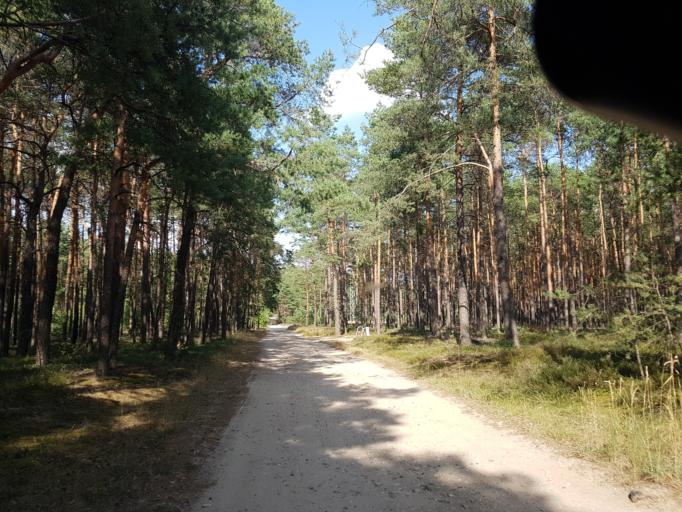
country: DE
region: Brandenburg
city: Finsterwalde
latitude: 51.6397
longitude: 13.7767
